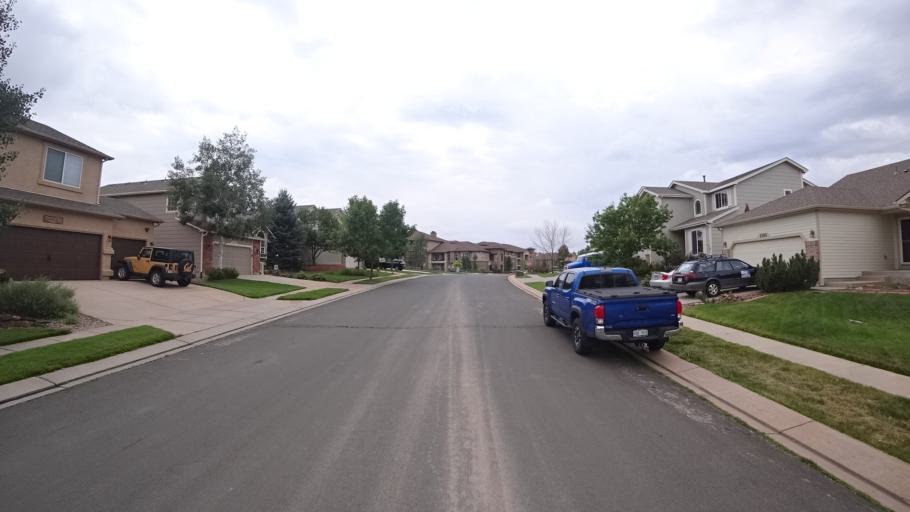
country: US
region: Colorado
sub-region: El Paso County
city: Gleneagle
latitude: 39.0049
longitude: -104.7988
